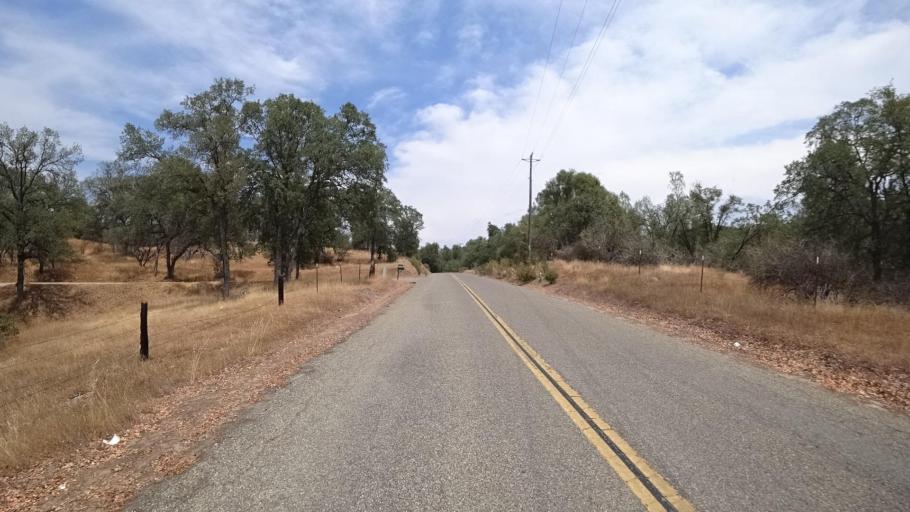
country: US
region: California
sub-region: Mariposa County
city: Mariposa
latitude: 37.4294
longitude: -119.8583
